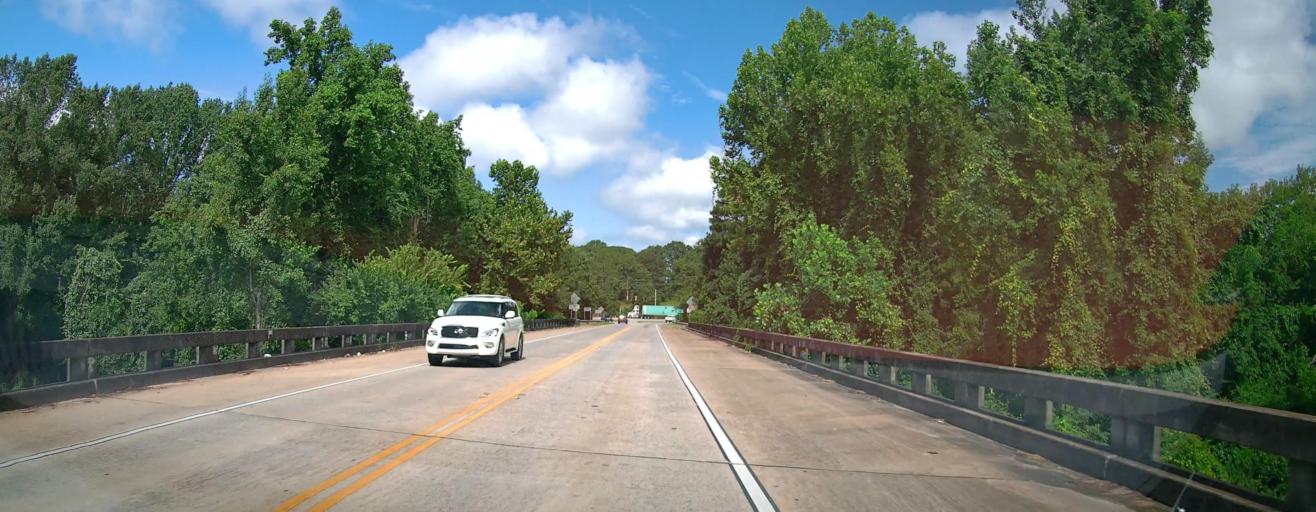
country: US
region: Georgia
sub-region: Peach County
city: Byron
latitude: 32.6070
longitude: -83.7913
